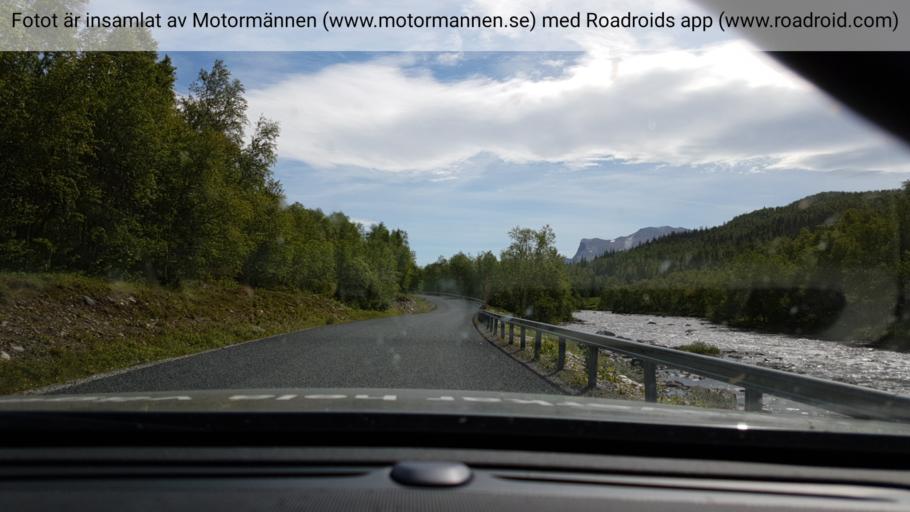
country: SE
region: Vaesterbotten
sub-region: Vilhelmina Kommun
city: Sjoberg
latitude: 65.2756
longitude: 15.3233
